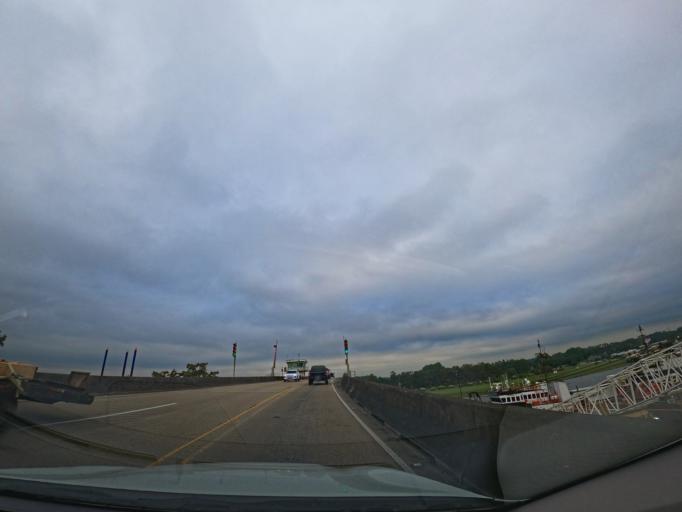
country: US
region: Louisiana
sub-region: Terrebonne Parish
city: Houma
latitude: 29.5676
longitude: -90.7200
